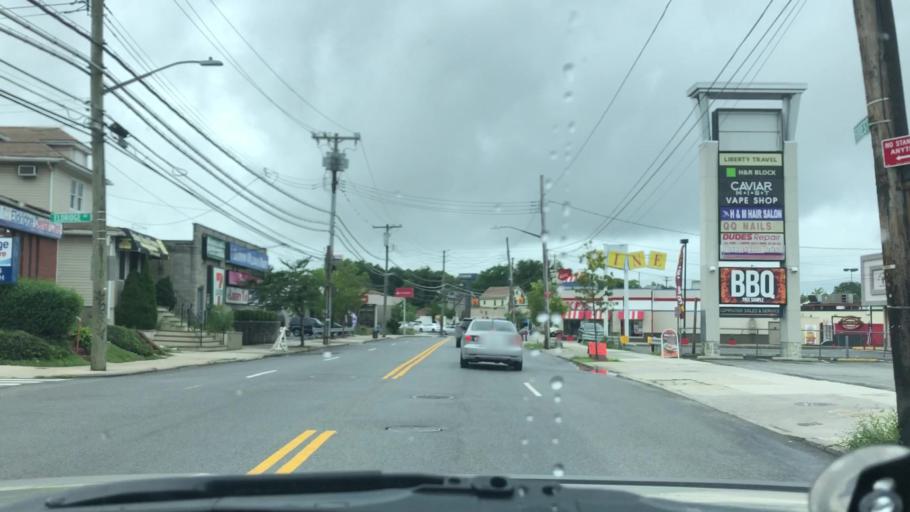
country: US
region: New York
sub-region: Richmond County
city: Bloomfield
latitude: 40.6249
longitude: -74.1361
